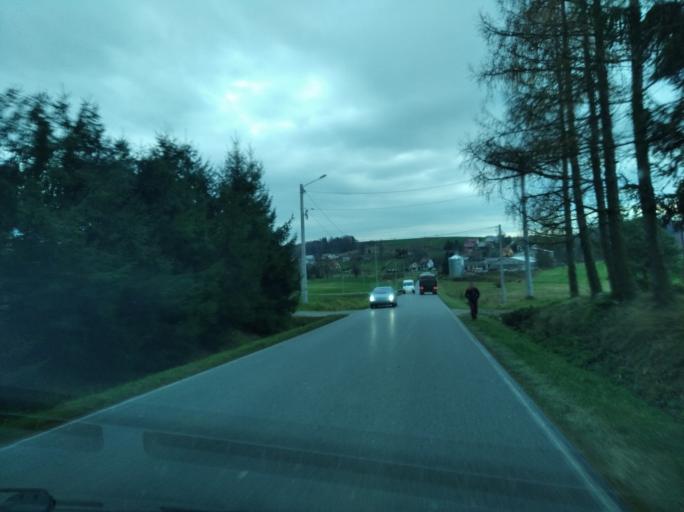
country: PL
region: Subcarpathian Voivodeship
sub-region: Powiat strzyzowski
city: Wisniowa
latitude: 49.9185
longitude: 21.7193
